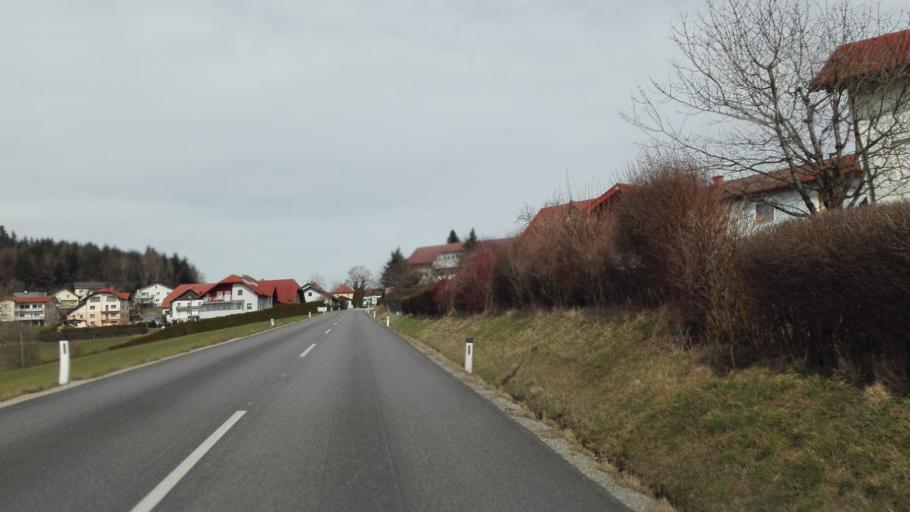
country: DE
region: Bavaria
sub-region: Lower Bavaria
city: Passau
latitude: 48.5150
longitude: 13.4918
